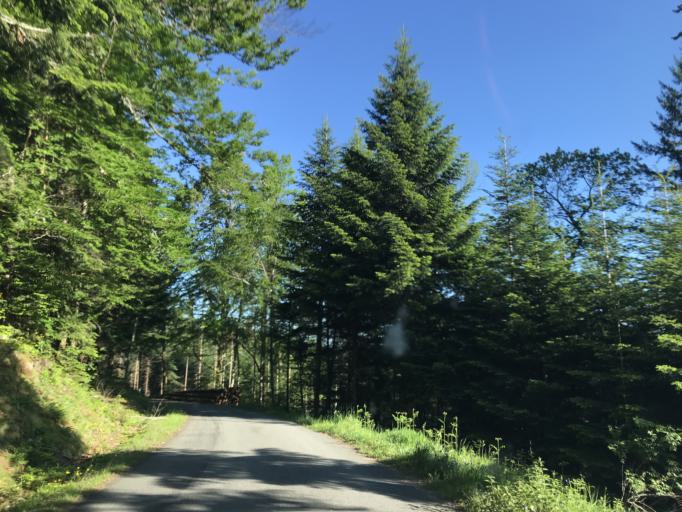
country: FR
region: Auvergne
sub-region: Departement du Puy-de-Dome
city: Job
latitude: 45.7054
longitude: 3.7080
